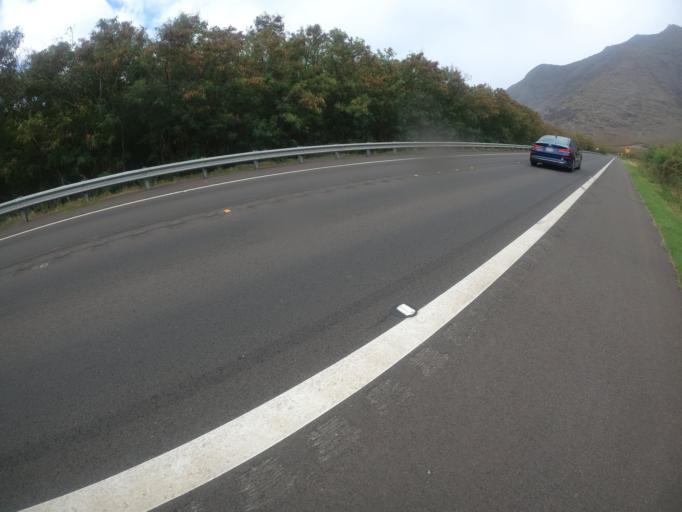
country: US
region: Hawaii
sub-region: Honolulu County
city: Makaha Valley
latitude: 21.5314
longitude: -158.2282
